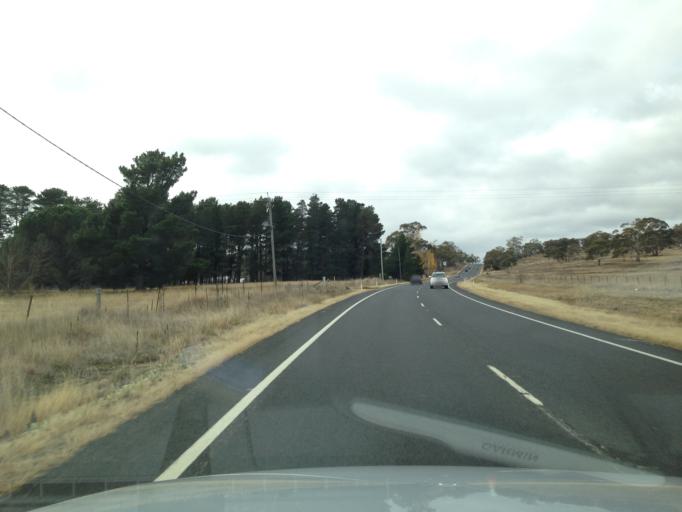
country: AU
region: New South Wales
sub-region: Cooma-Monaro
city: Cooma
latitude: -36.2412
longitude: 149.0665
